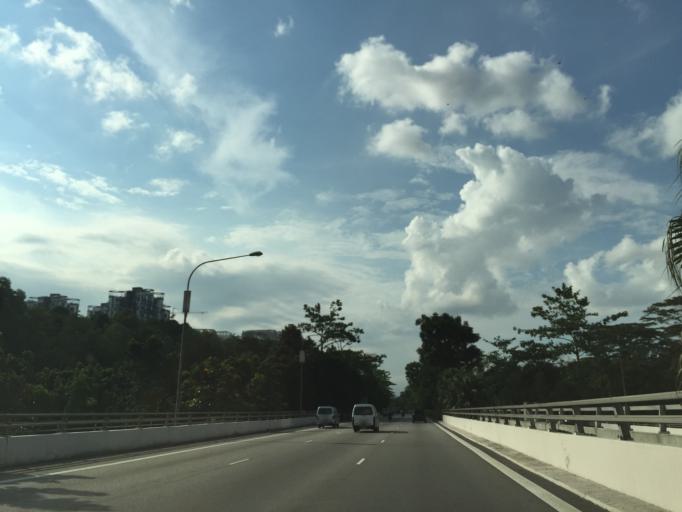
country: MY
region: Johor
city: Johor Bahru
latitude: 1.3651
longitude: 103.7796
